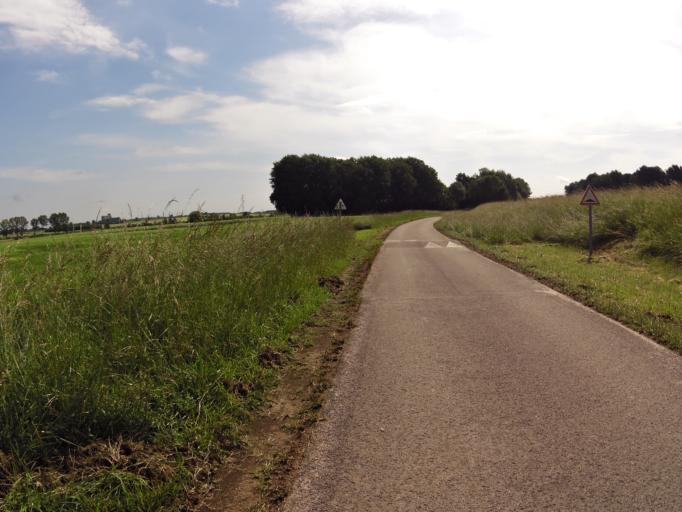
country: FR
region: Champagne-Ardenne
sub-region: Departement de l'Aube
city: Verrieres
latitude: 48.2725
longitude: 4.1542
